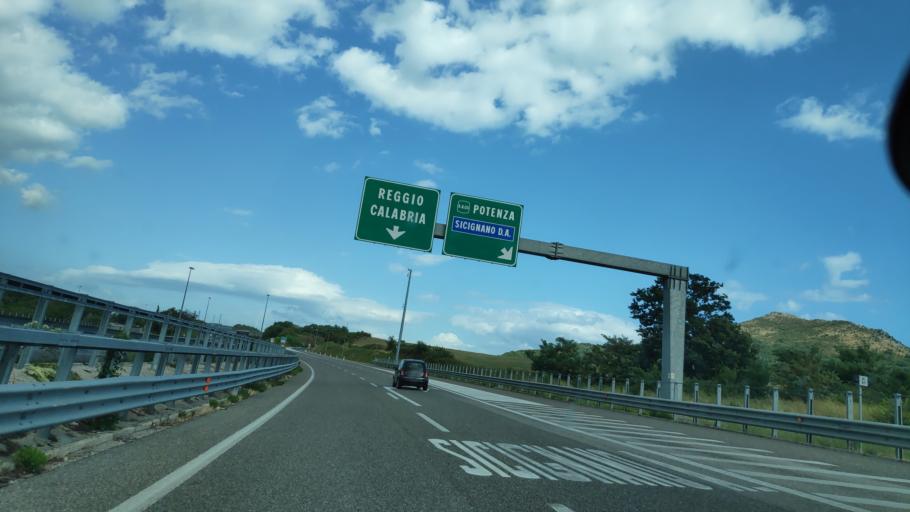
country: IT
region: Campania
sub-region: Provincia di Salerno
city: Palomonte
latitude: 40.6106
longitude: 15.2864
